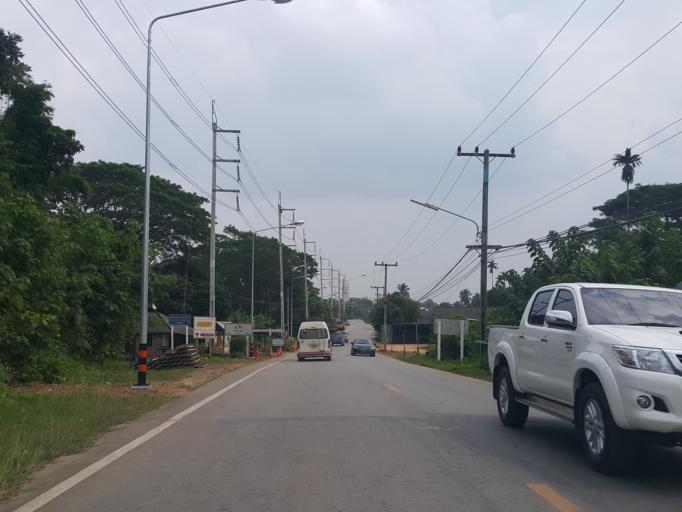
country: TH
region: Chiang Mai
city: Mae Taeng
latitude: 19.0973
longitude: 98.8462
